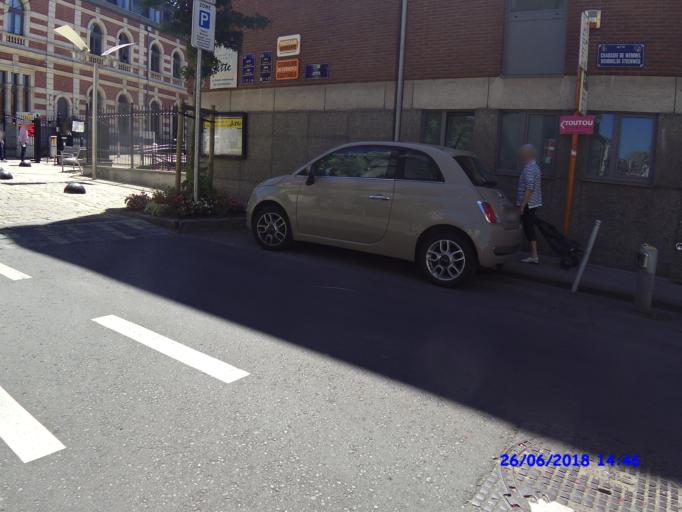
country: BE
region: Brussels Capital
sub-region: Bruxelles-Capitale
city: Brussels
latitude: 50.8762
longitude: 4.3246
